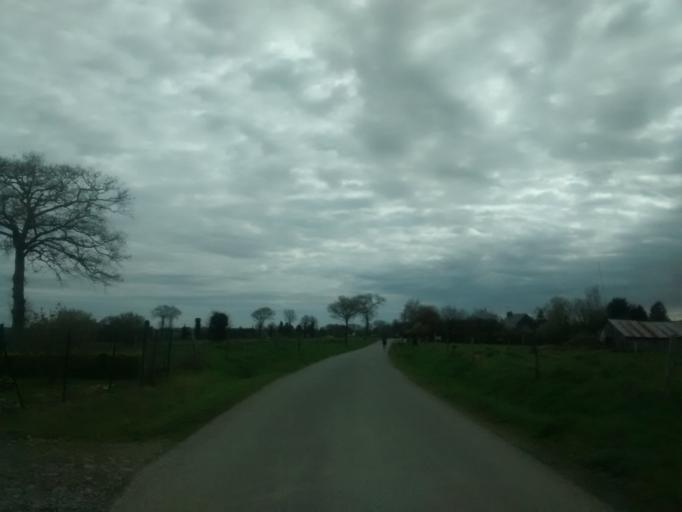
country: FR
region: Brittany
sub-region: Departement d'Ille-et-Vilaine
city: Erce-pres-Liffre
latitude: 48.2442
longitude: -1.5167
